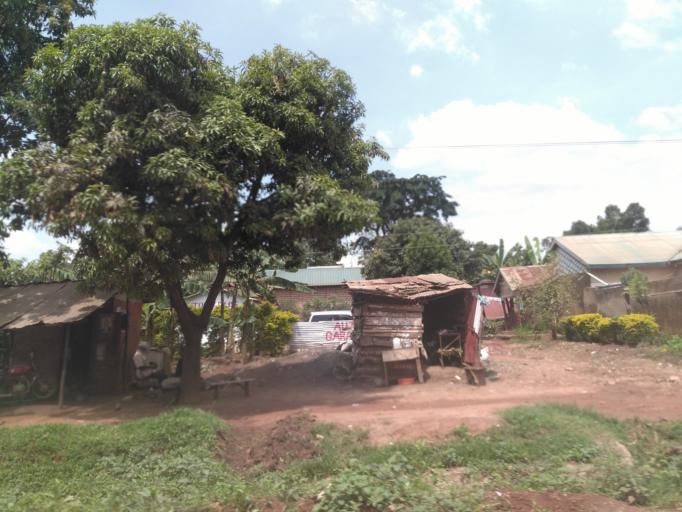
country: UG
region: Central Region
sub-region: Wakiso District
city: Bweyogerere
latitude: 0.4531
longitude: 32.6135
